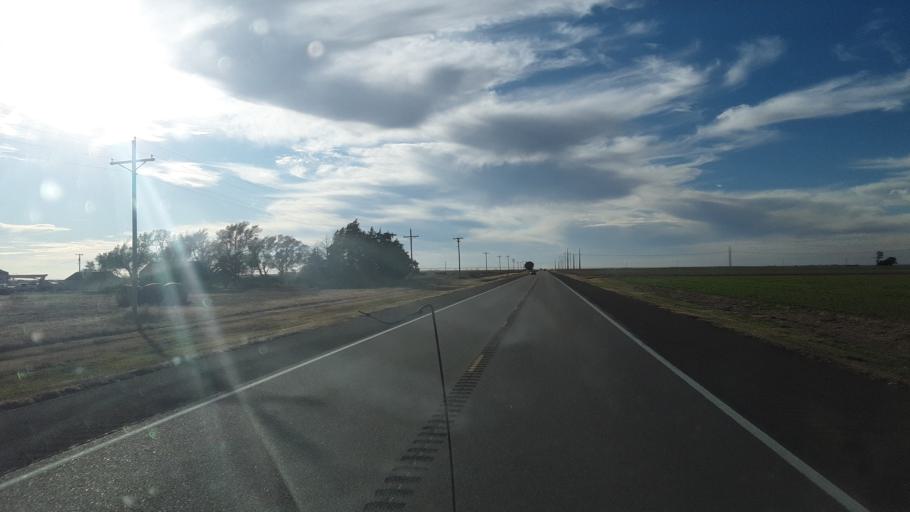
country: US
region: Kansas
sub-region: Finney County
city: Holcomb
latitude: 38.0034
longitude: -101.0552
